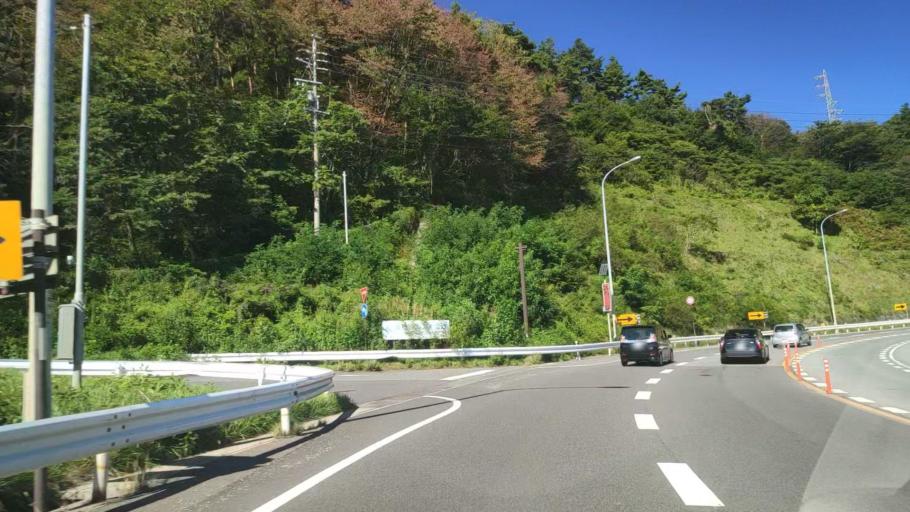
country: JP
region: Nagano
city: Okaya
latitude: 36.0818
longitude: 138.0309
